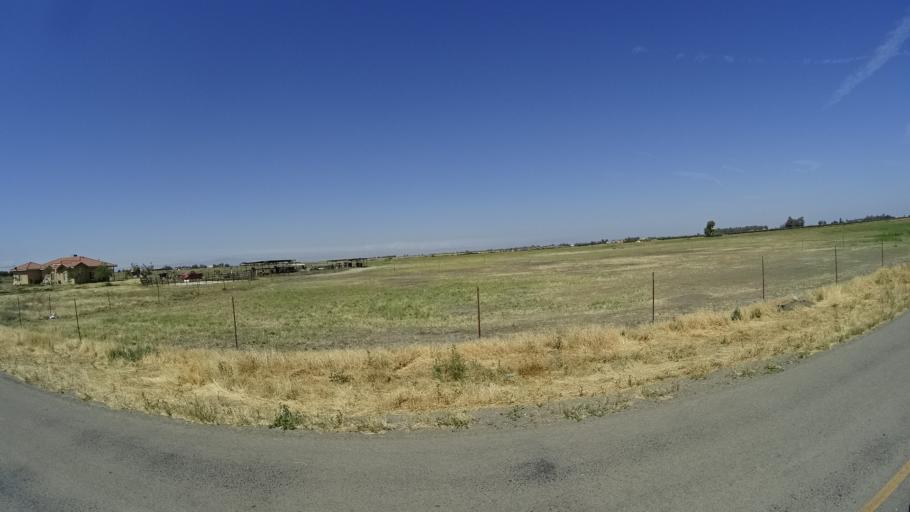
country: US
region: California
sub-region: Kings County
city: Stratford
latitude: 36.1803
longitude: -119.7803
